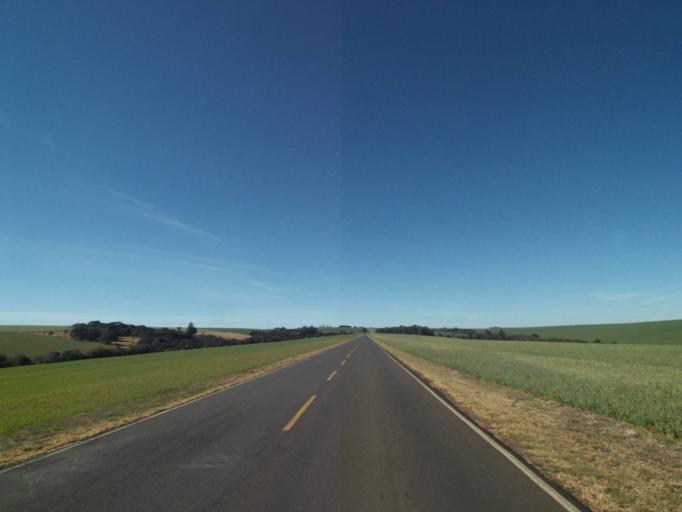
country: BR
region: Parana
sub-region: Tibagi
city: Tibagi
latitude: -24.5274
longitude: -50.3226
